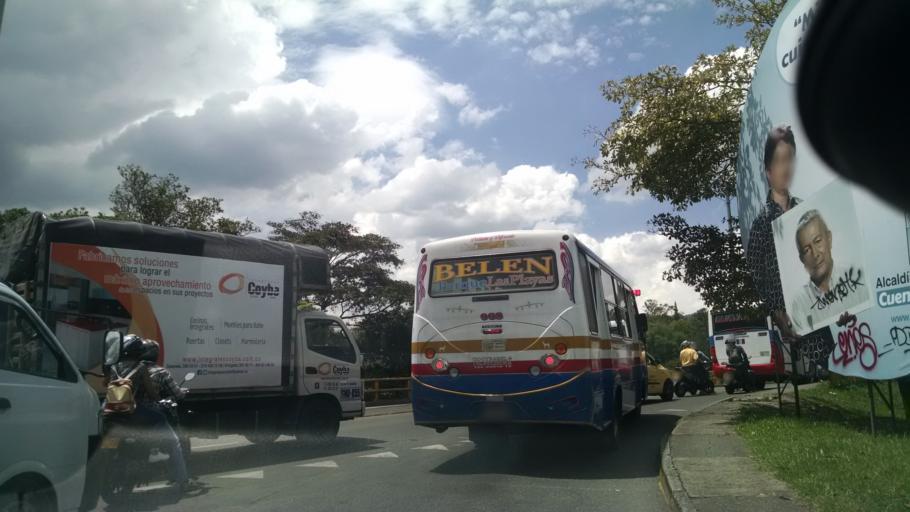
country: CO
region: Antioquia
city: Itagui
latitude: 6.2041
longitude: -75.5865
